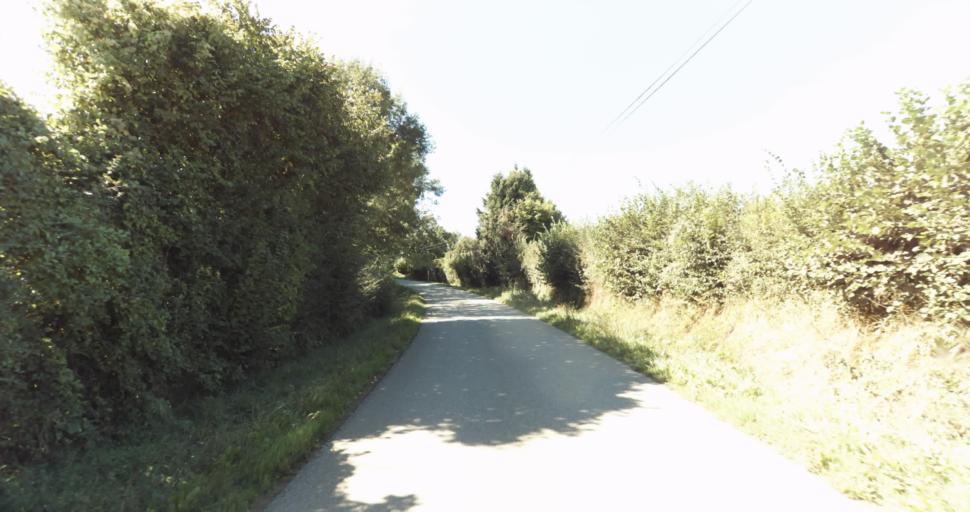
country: FR
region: Lower Normandy
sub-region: Departement de l'Orne
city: Gace
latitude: 48.7842
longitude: 0.2811
